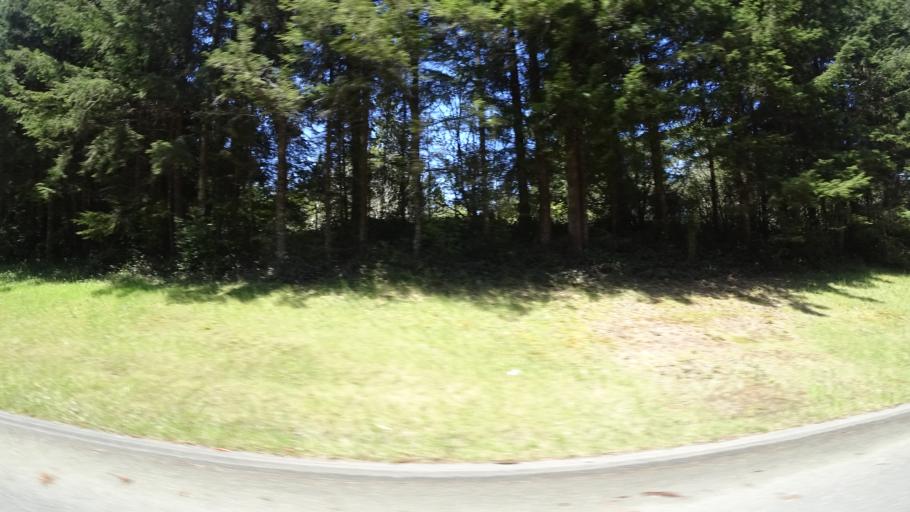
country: US
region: California
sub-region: Humboldt County
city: Westhaven-Moonstone
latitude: 41.1041
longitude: -124.1547
